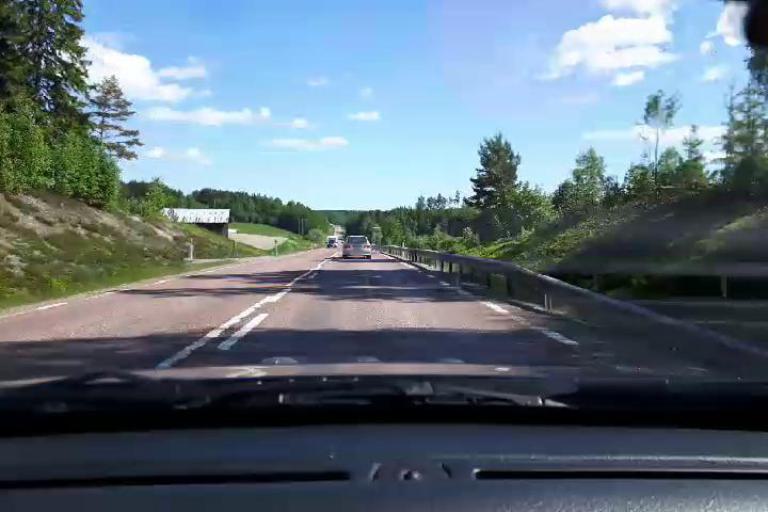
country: SE
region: Gaevleborg
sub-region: Hudiksvalls Kommun
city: Sorforsa
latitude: 61.7485
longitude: 16.8383
